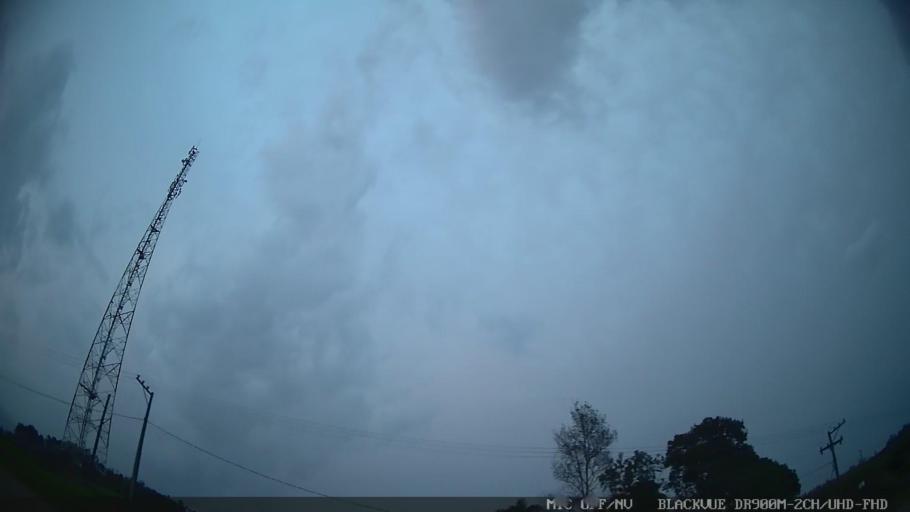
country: BR
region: Sao Paulo
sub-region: Braganca Paulista
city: Braganca Paulista
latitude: -22.9430
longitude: -46.6358
